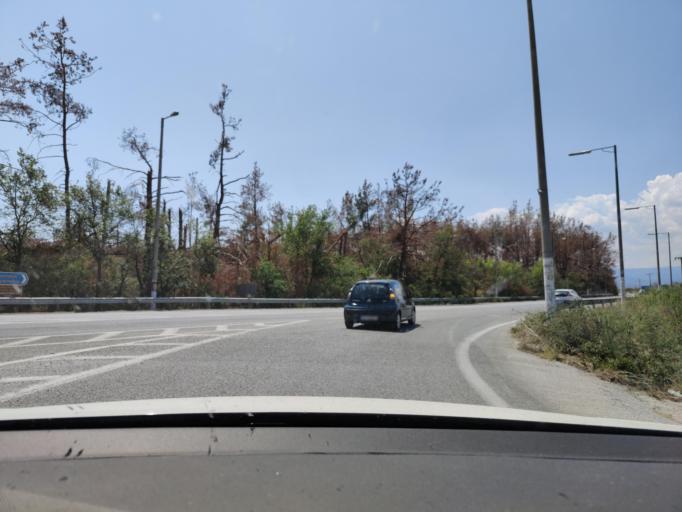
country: GR
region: Central Macedonia
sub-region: Nomos Serron
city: Palaiokomi
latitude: 40.8675
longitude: 23.8699
